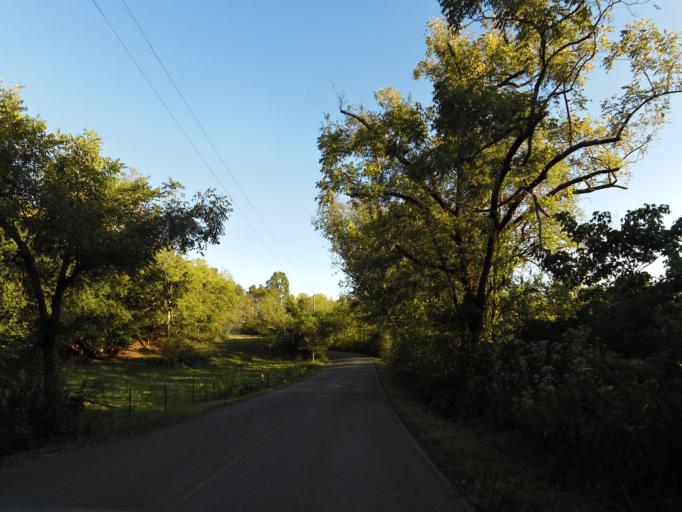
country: US
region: Tennessee
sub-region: Blount County
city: Eagleton Village
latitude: 35.8209
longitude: -83.9151
